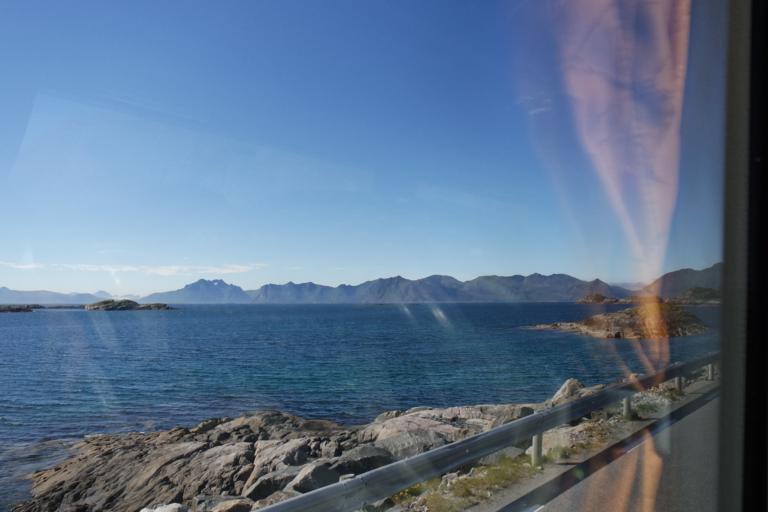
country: NO
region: Nordland
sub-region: Vagan
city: Kabelvag
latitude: 68.1600
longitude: 14.2153
